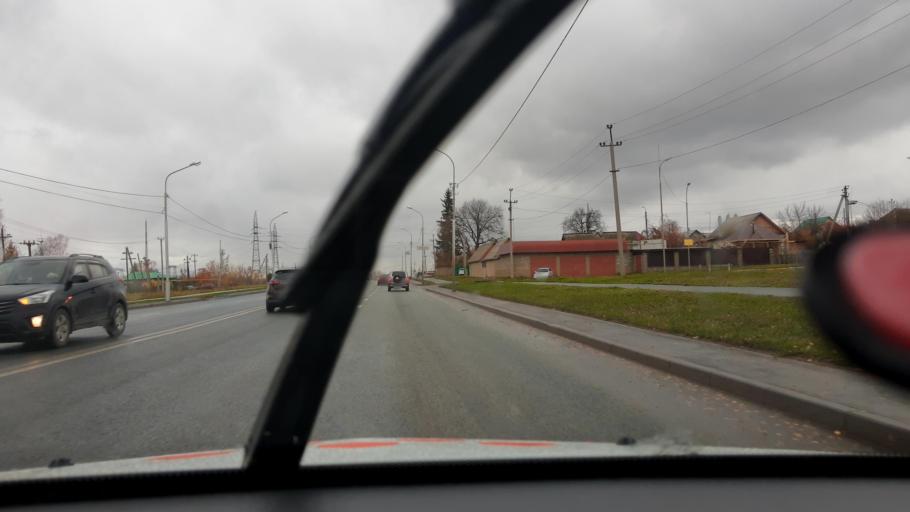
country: RU
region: Bashkortostan
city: Iglino
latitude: 54.7790
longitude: 56.2285
